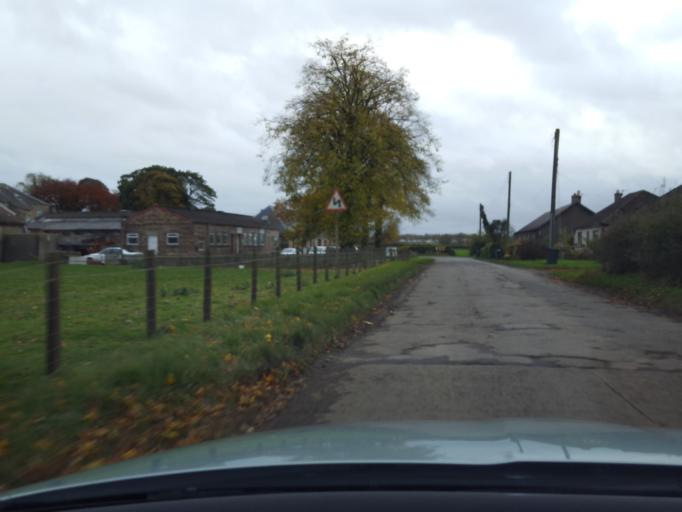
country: GB
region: Scotland
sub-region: West Lothian
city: East Calder
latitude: 55.9053
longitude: -3.4405
